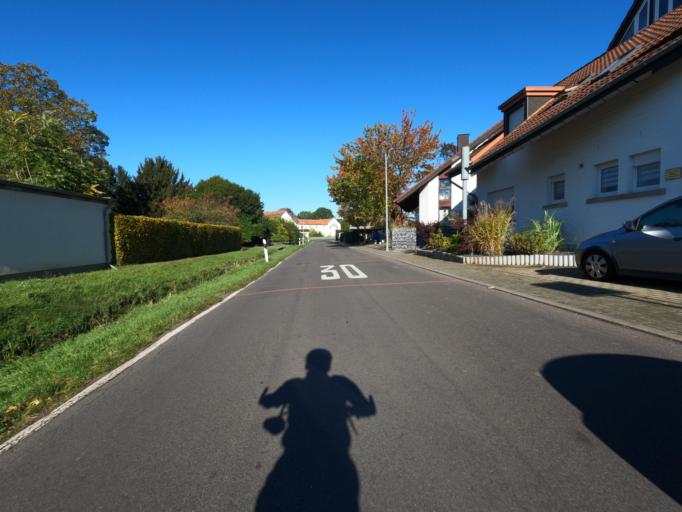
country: DE
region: North Rhine-Westphalia
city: Huckelhoven
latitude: 51.0456
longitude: 6.2465
